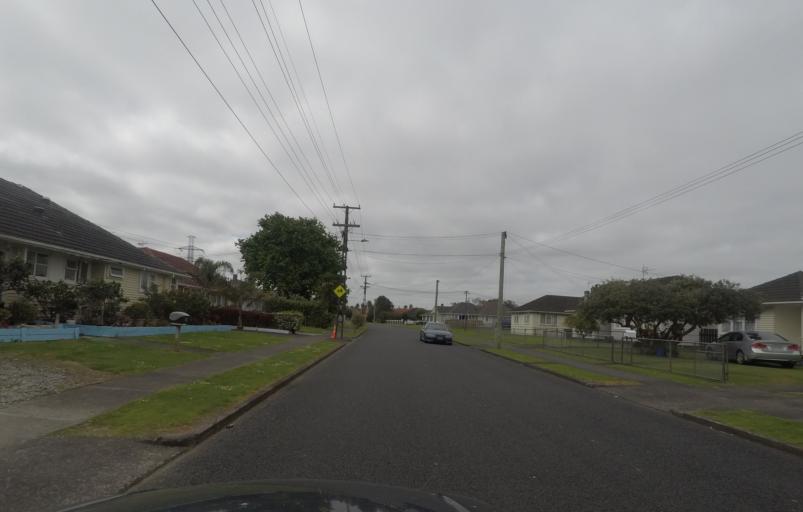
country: NZ
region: Auckland
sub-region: Auckland
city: Manukau City
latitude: -36.9607
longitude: 174.8664
